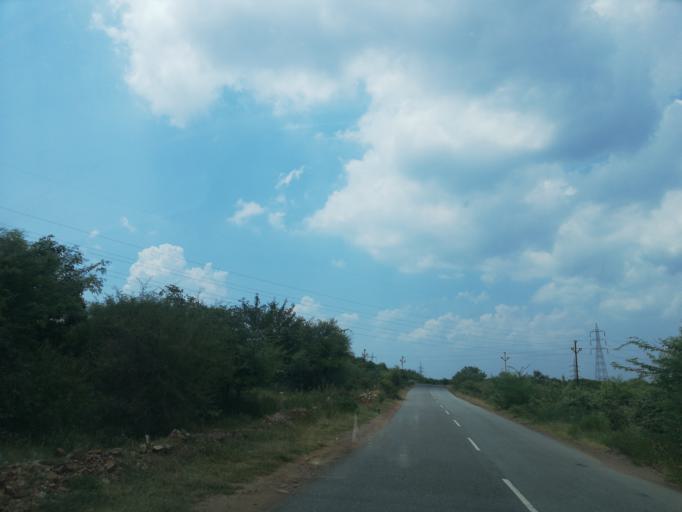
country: IN
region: Andhra Pradesh
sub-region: Guntur
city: Macherla
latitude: 16.5634
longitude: 79.3501
